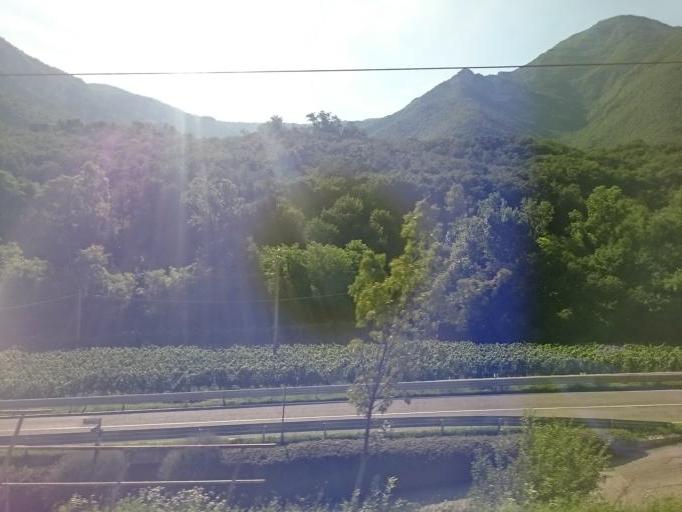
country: IT
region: Veneto
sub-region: Provincia di Verona
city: Dolce
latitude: 45.6075
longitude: 10.8566
